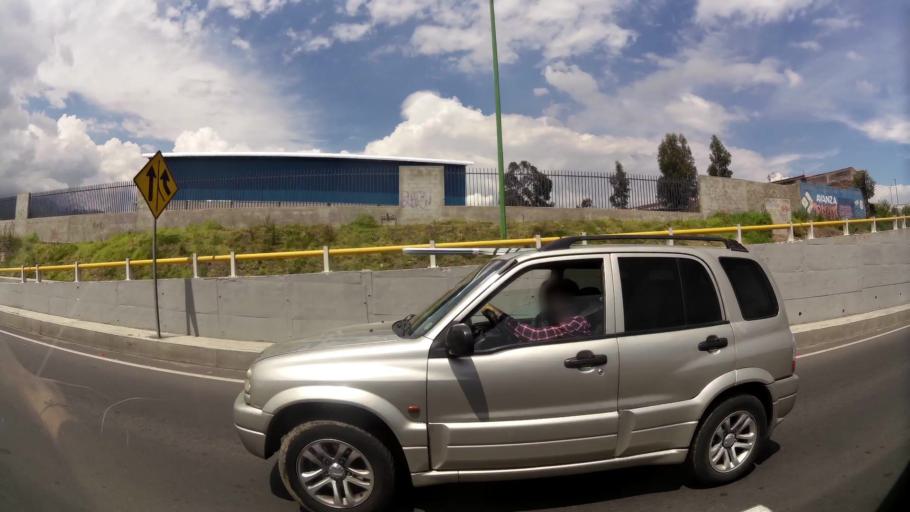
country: EC
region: Pichincha
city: Sangolqui
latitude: -0.2248
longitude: -78.3463
